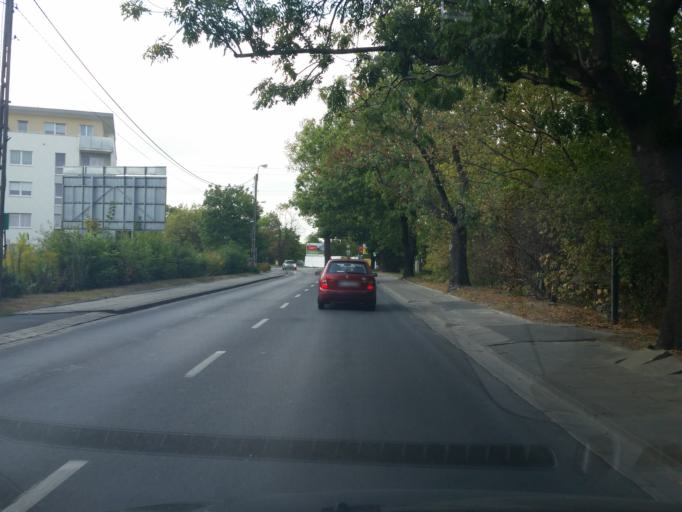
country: PL
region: Masovian Voivodeship
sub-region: Warszawa
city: Ursus
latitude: 52.1984
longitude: 20.8762
